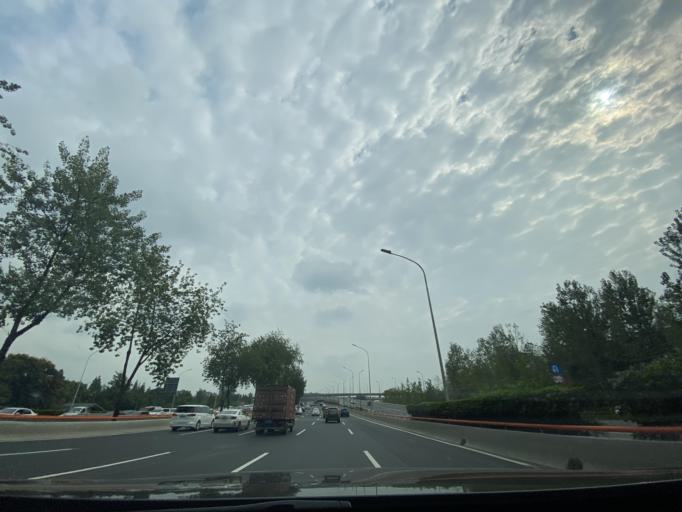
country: CN
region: Sichuan
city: Chengdu
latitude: 30.6631
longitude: 103.9826
